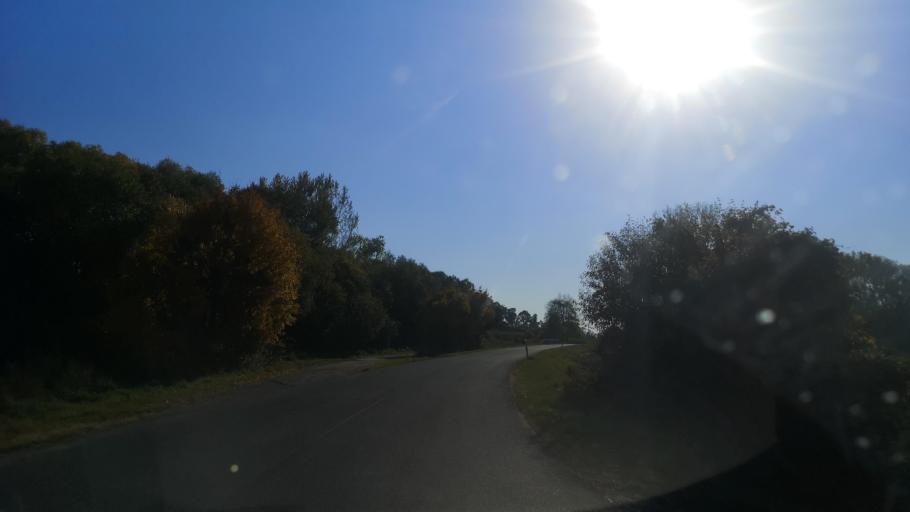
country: SK
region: Nitriansky
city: Zlate Moravce
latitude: 48.4341
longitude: 18.4299
